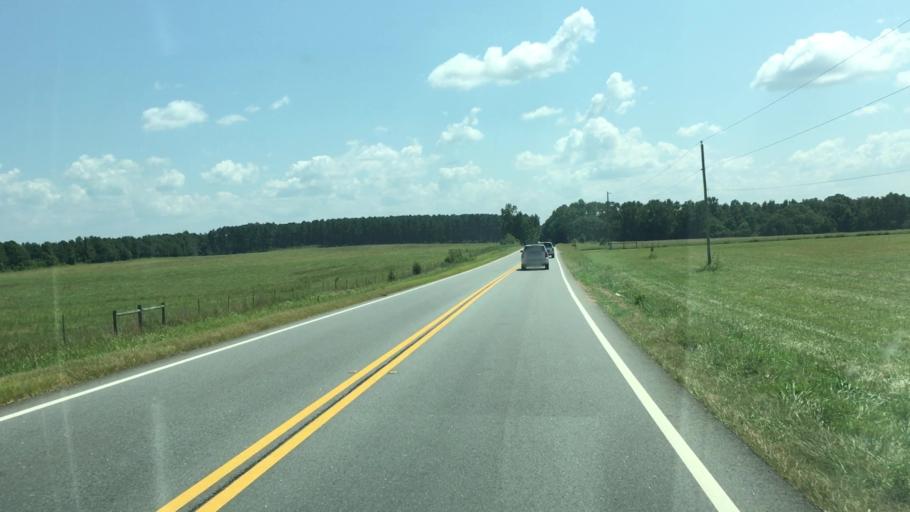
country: US
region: Georgia
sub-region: Oconee County
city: Watkinsville
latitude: 33.7976
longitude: -83.4255
